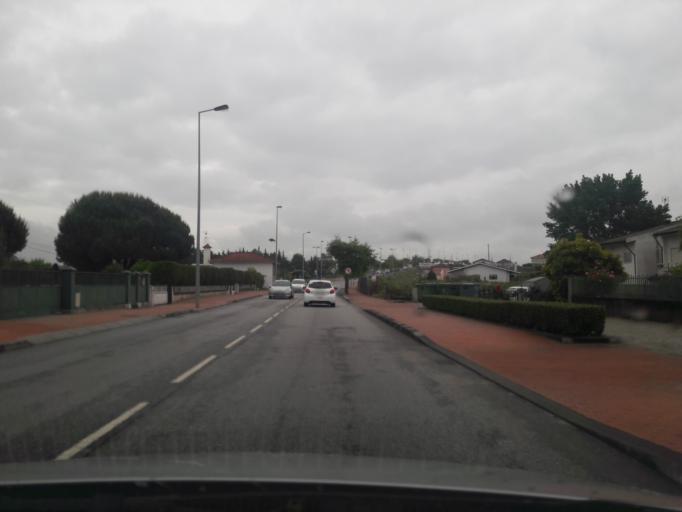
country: PT
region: Porto
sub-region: Vila do Conde
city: Arvore
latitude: 41.3362
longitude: -8.7242
